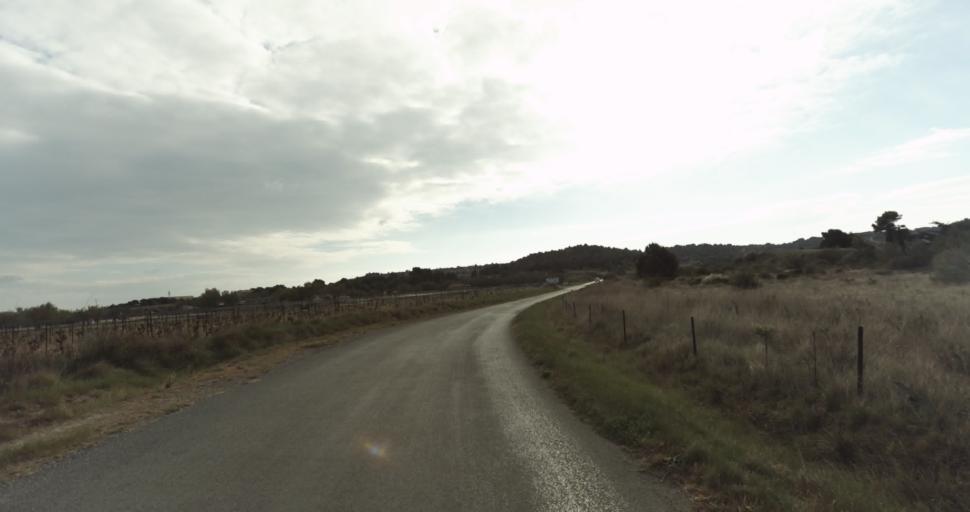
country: FR
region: Languedoc-Roussillon
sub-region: Departement de l'Aude
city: Leucate
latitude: 42.9300
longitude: 3.0066
